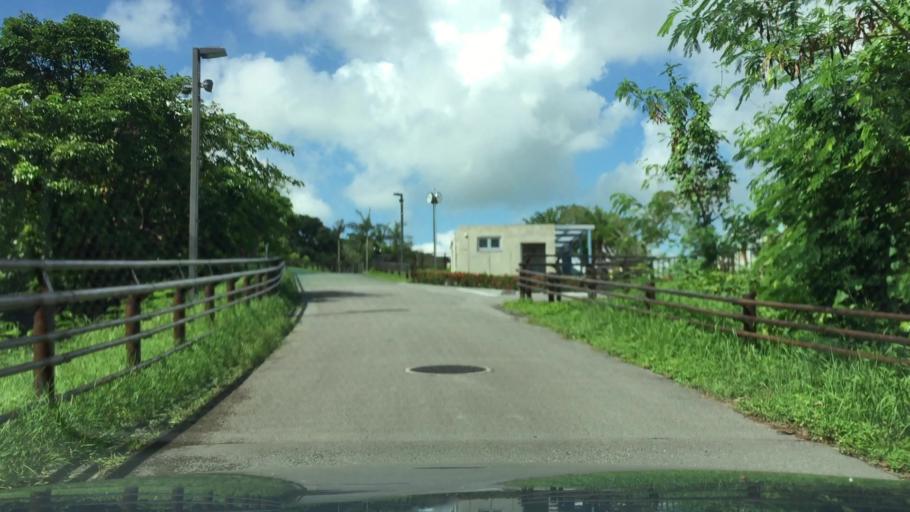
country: JP
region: Okinawa
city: Ishigaki
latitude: 24.3857
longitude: 124.1608
